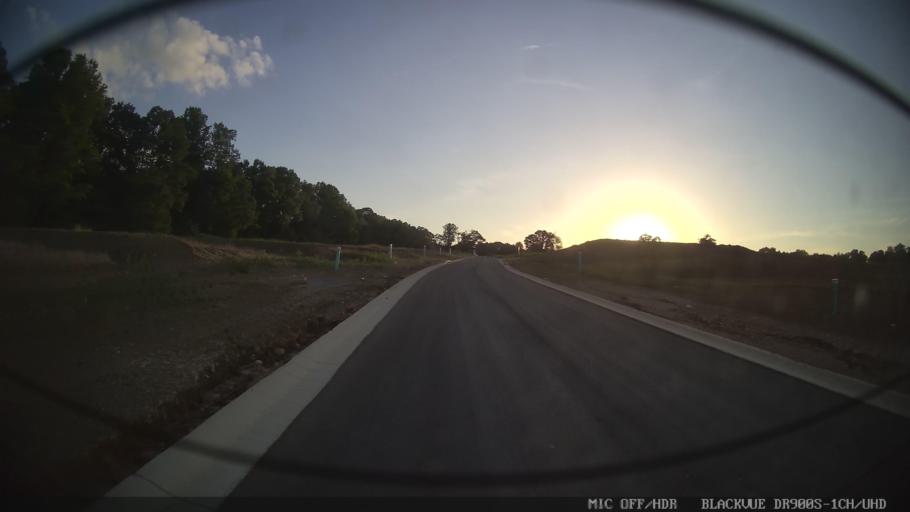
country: US
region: Georgia
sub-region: Forsyth County
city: Cumming
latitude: 34.2194
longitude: -84.2144
